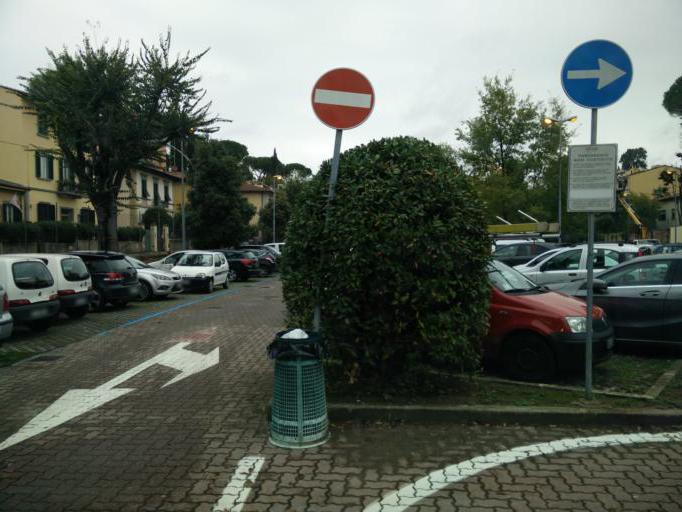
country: IT
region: Tuscany
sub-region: Province of Florence
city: Florence
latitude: 43.7518
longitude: 11.2441
